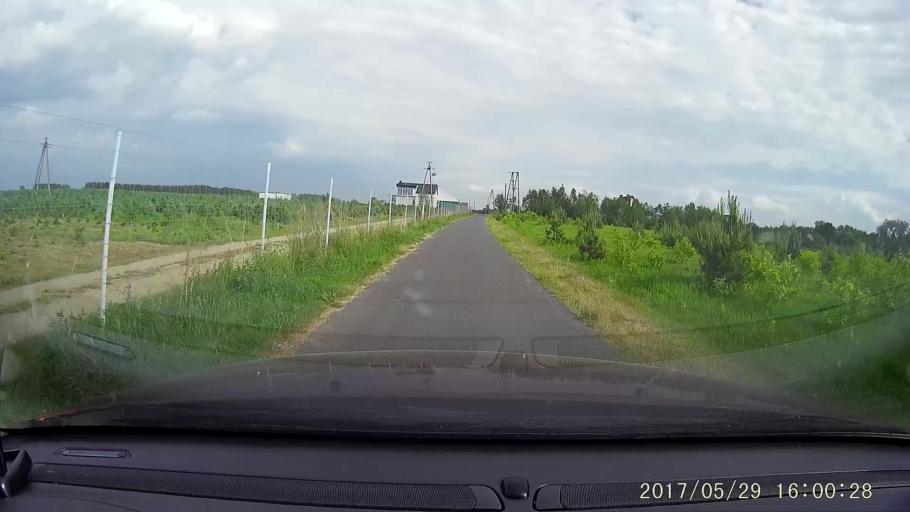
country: PL
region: Lower Silesian Voivodeship
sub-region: Powiat zgorzelecki
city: Wegliniec
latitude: 51.2371
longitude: 15.1978
